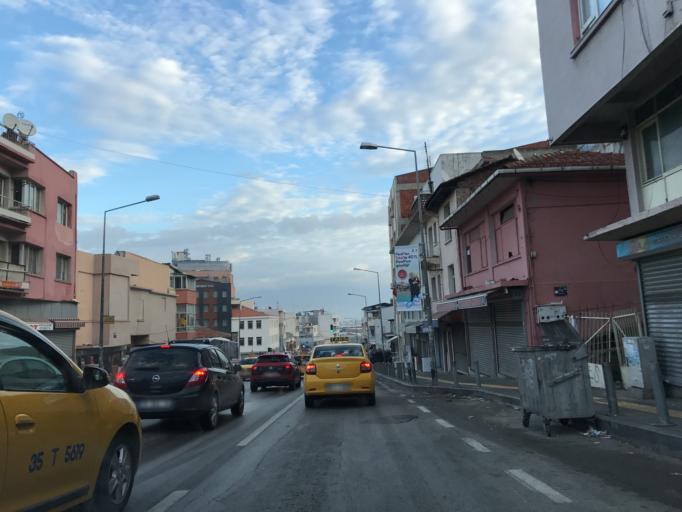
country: TR
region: Izmir
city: Izmir
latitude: 38.4153
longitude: 27.1348
